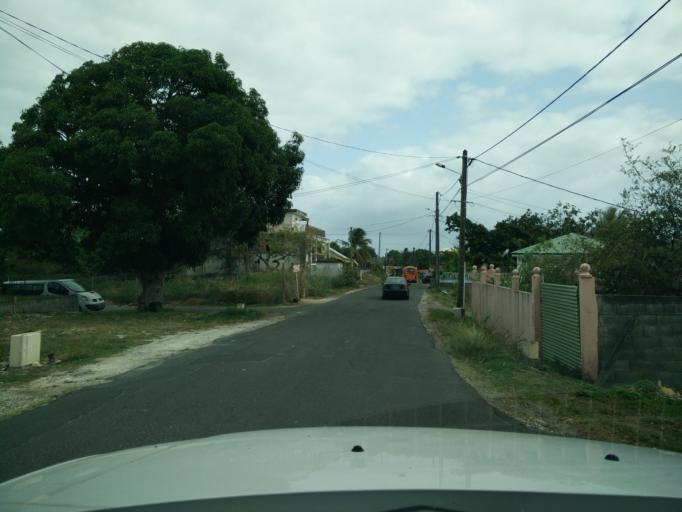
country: GP
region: Guadeloupe
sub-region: Guadeloupe
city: Sainte-Anne
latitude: 16.2189
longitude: -61.4323
